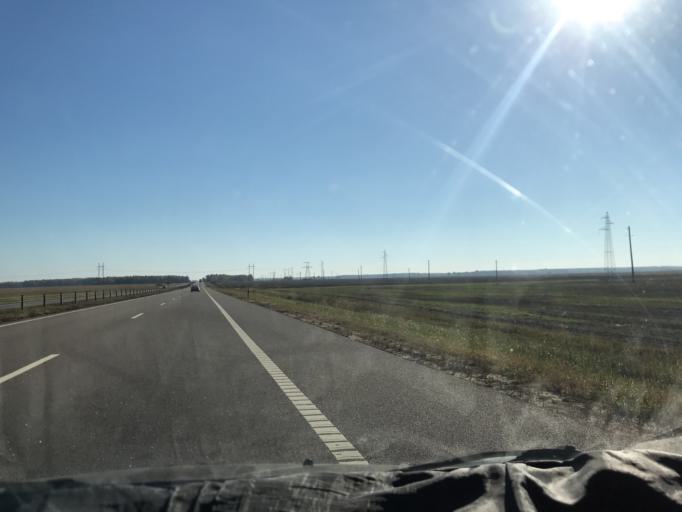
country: BY
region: Mogilev
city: Yalizava
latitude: 53.2319
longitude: 28.9846
